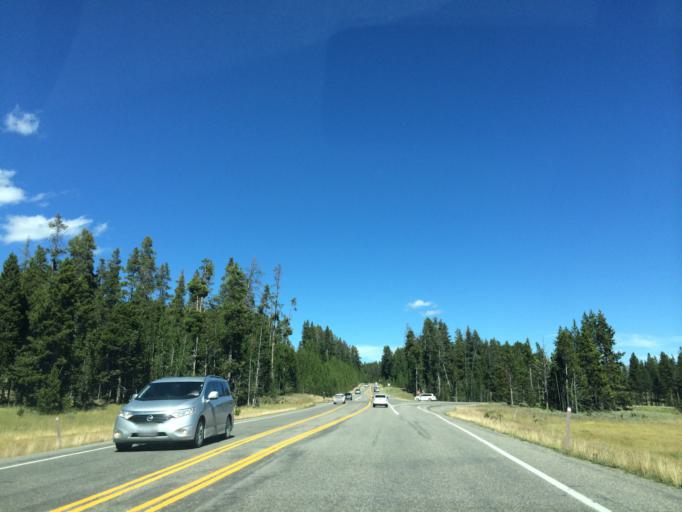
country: US
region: Montana
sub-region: Gallatin County
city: West Yellowstone
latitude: 44.5670
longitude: -110.3892
